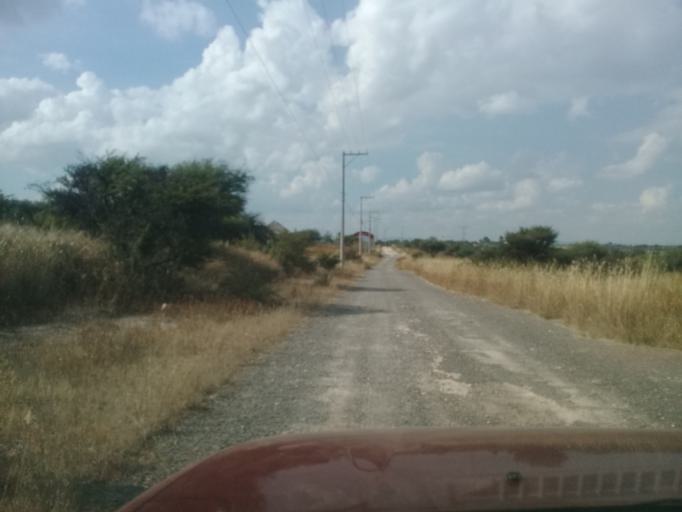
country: MX
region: Aguascalientes
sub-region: Aguascalientes
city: San Sebastian [Fraccionamiento]
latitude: 21.7813
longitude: -102.3282
